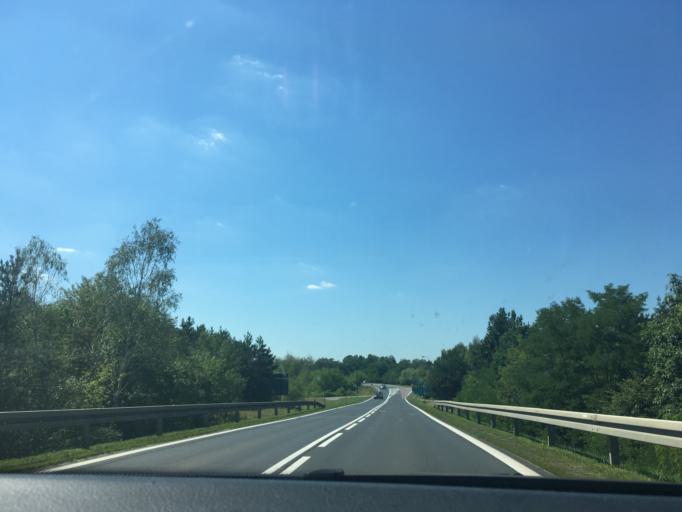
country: PL
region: Subcarpathian Voivodeship
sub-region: Powiat nizanski
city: Nisko
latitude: 50.5099
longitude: 22.1462
